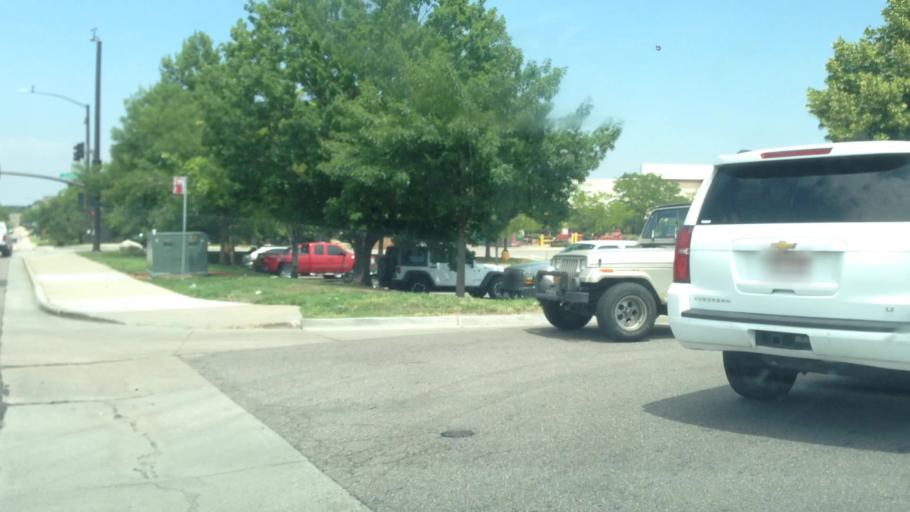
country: US
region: Colorado
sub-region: Arapahoe County
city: Centennial
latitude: 39.5963
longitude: -104.8808
